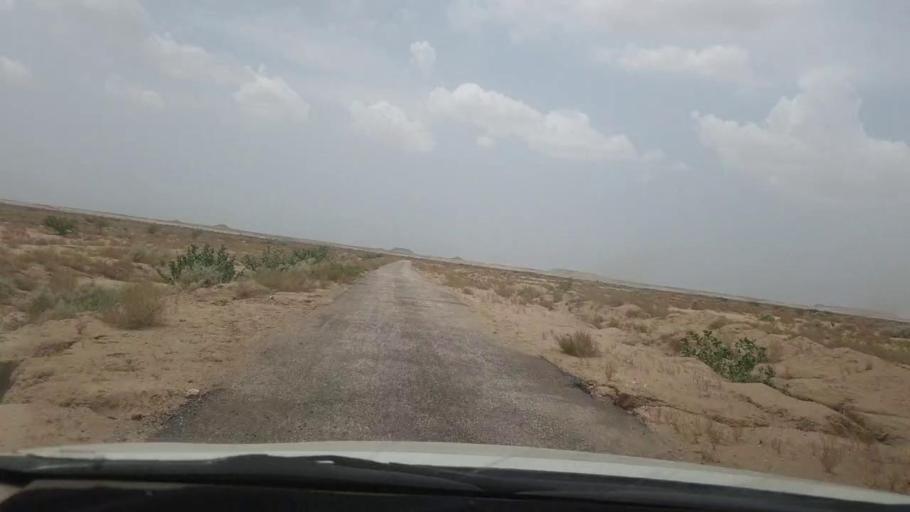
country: PK
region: Sindh
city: Khairpur
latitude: 27.4016
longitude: 68.9684
